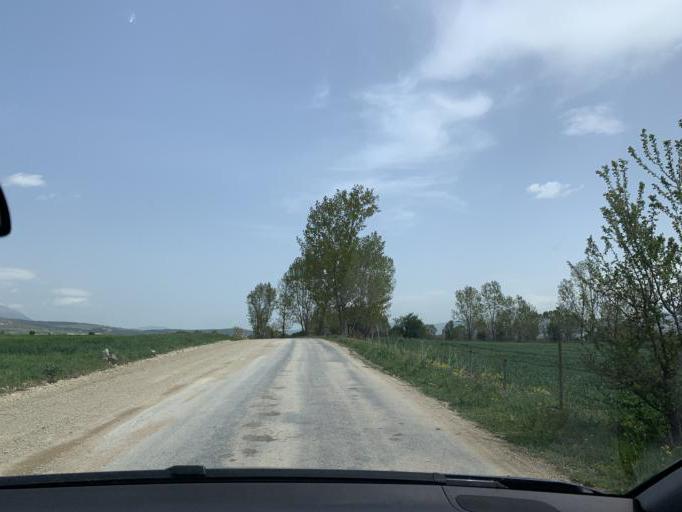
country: TR
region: Bolu
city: Bolu
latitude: 40.7489
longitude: 31.6668
